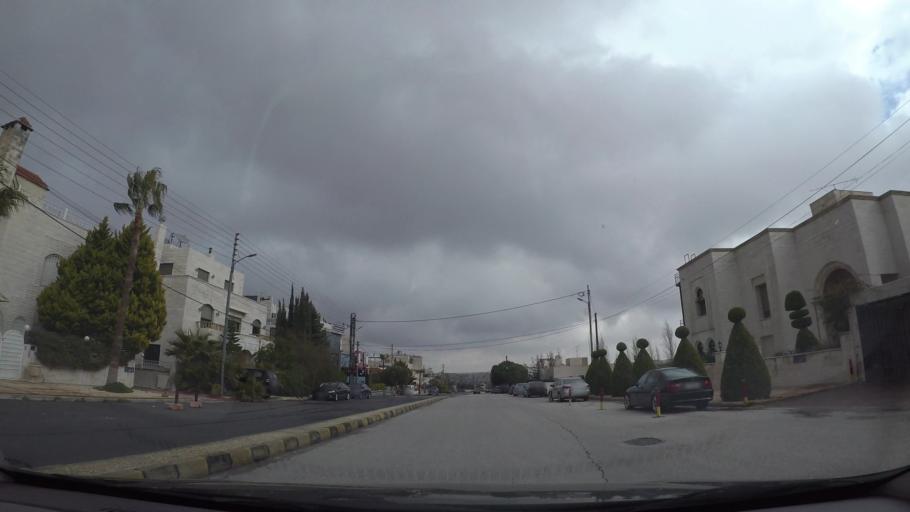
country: JO
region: Amman
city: Al Bunayyat ash Shamaliyah
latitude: 31.9408
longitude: 35.8919
